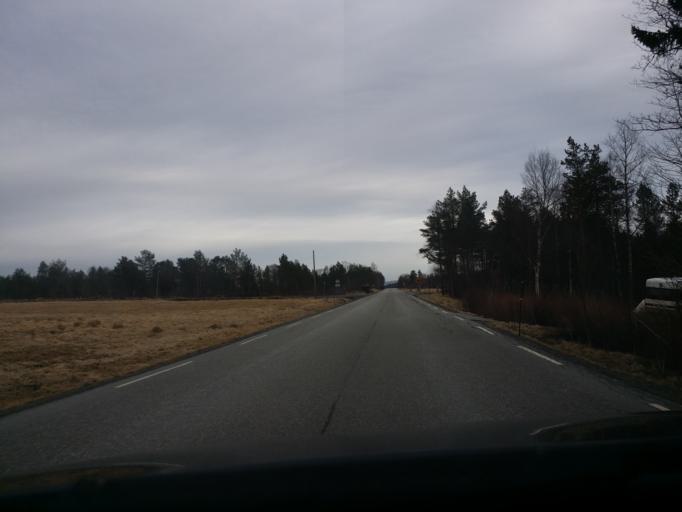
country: NO
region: More og Romsdal
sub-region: Halsa
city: Liaboen
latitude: 63.1223
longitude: 8.3356
